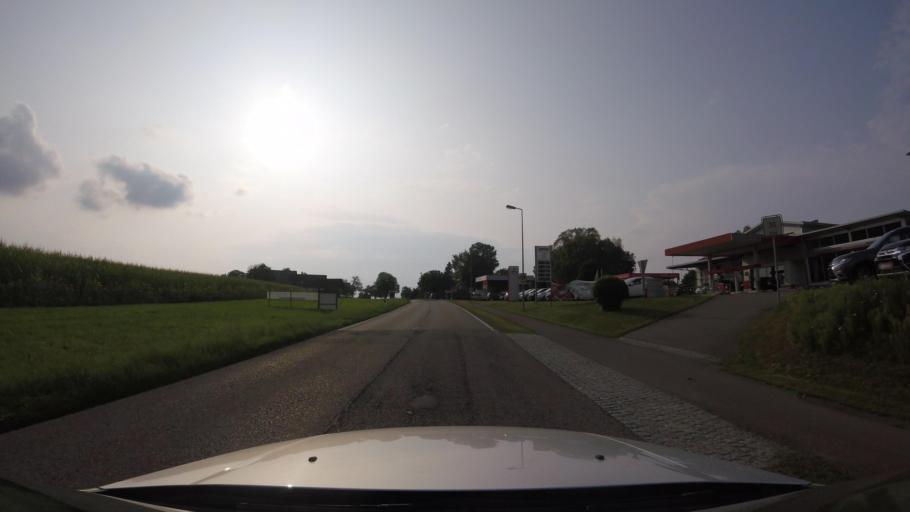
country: DE
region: Baden-Wuerttemberg
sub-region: Regierungsbezirk Stuttgart
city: Alfdorf
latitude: 48.8425
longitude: 9.6762
